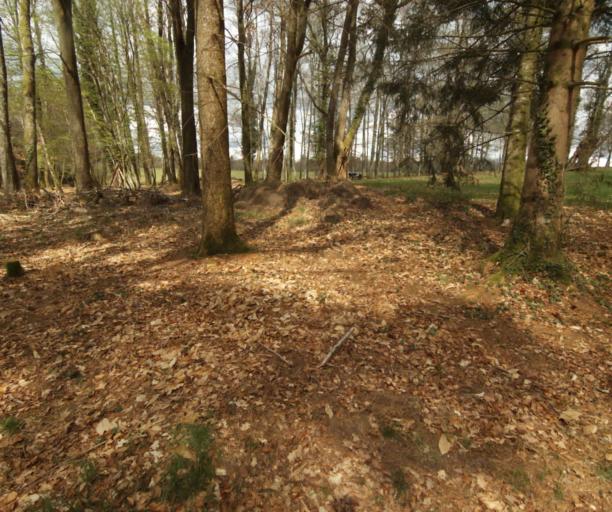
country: FR
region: Limousin
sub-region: Departement de la Correze
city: Laguenne
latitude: 45.2538
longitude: 1.9006
